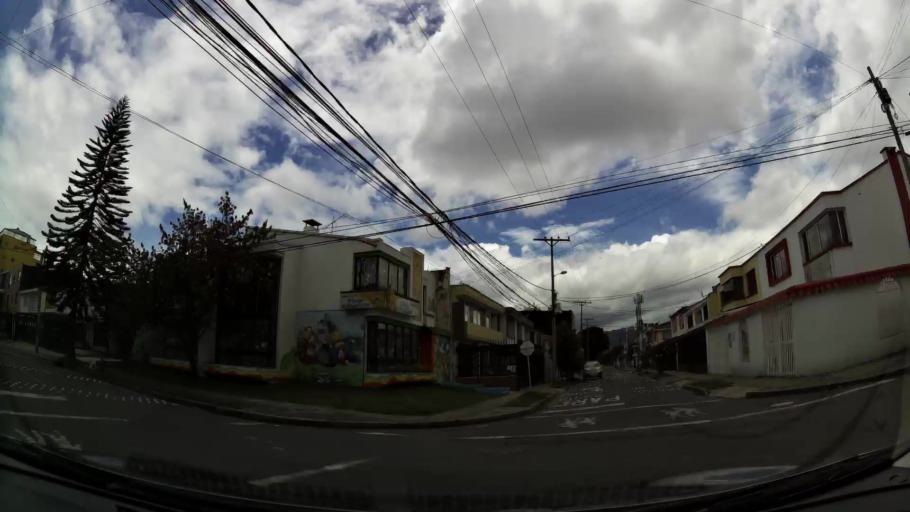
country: CO
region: Bogota D.C.
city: Bogota
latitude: 4.6673
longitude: -74.1092
